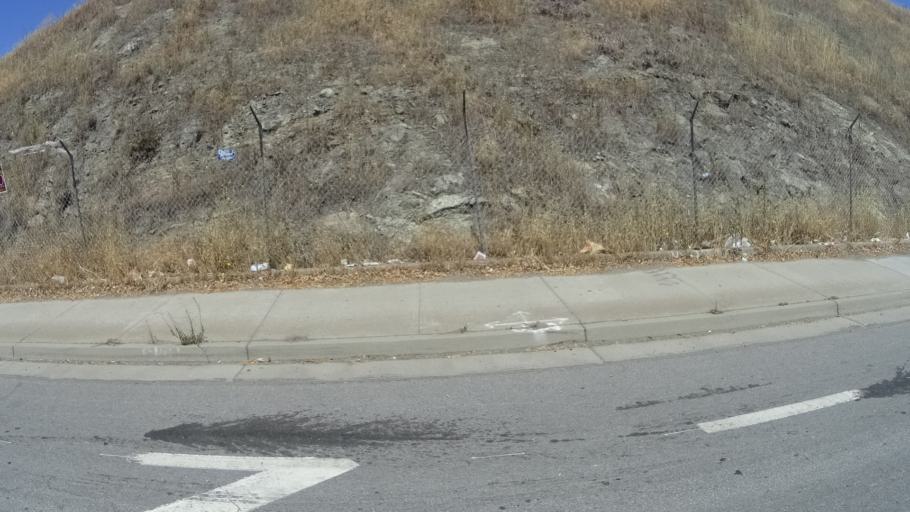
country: US
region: California
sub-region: Santa Clara County
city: Seven Trees
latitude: 37.2747
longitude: -121.8317
